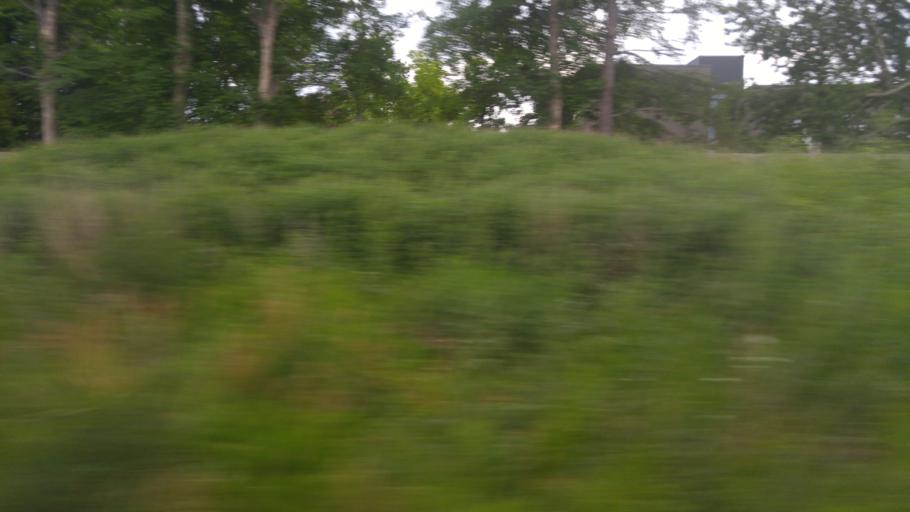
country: NO
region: Sor-Trondelag
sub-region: Trondheim
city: Trondheim
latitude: 63.4401
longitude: 10.4510
